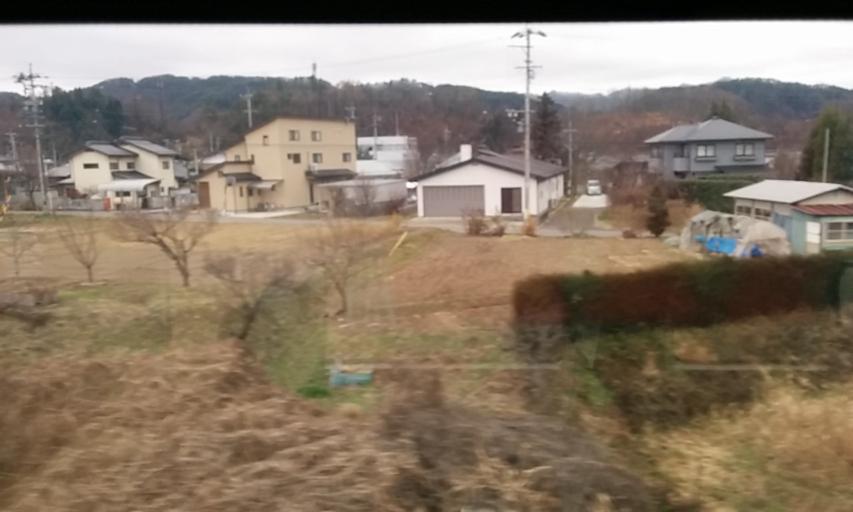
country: JP
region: Nagano
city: Hotaka
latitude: 36.4054
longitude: 138.0148
